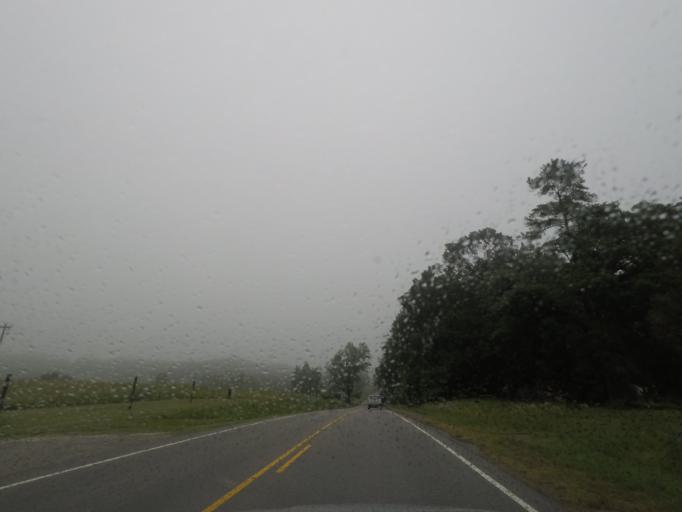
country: US
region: Virginia
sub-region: Prince Edward County
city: Farmville
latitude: 37.3834
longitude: -78.4848
